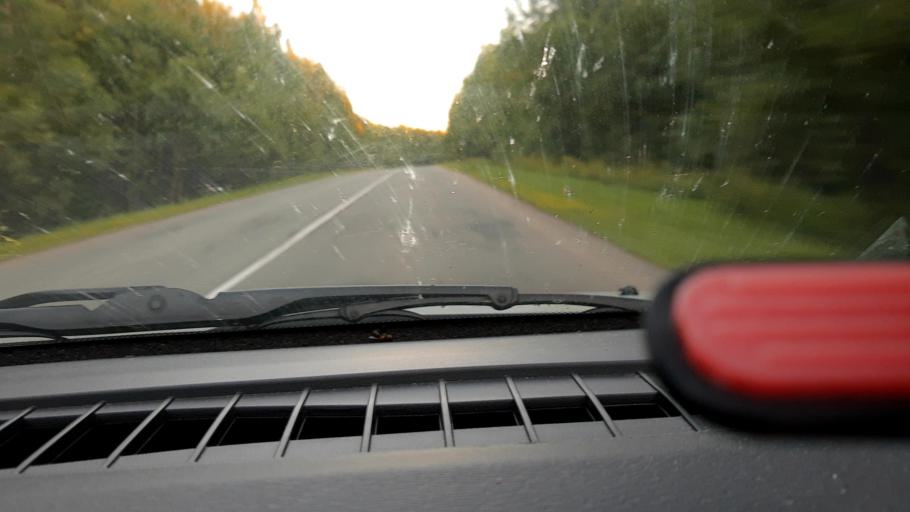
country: RU
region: Nizjnij Novgorod
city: Tonkino
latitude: 57.3351
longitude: 46.4764
